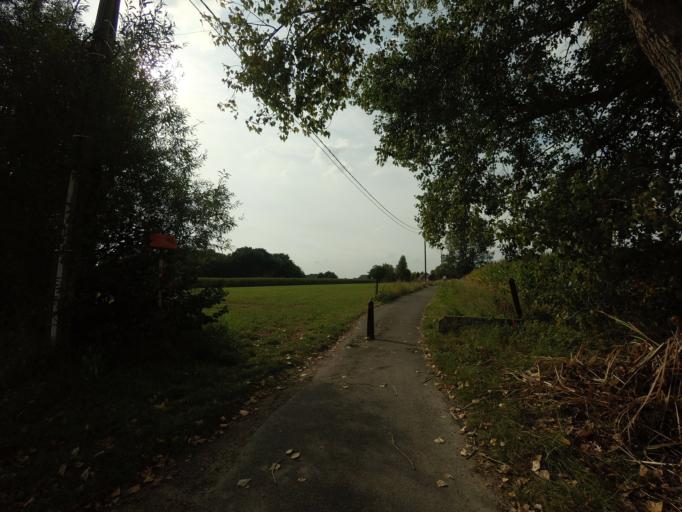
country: BE
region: Flanders
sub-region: Provincie Antwerpen
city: Aartselaar
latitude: 51.1304
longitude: 4.4071
